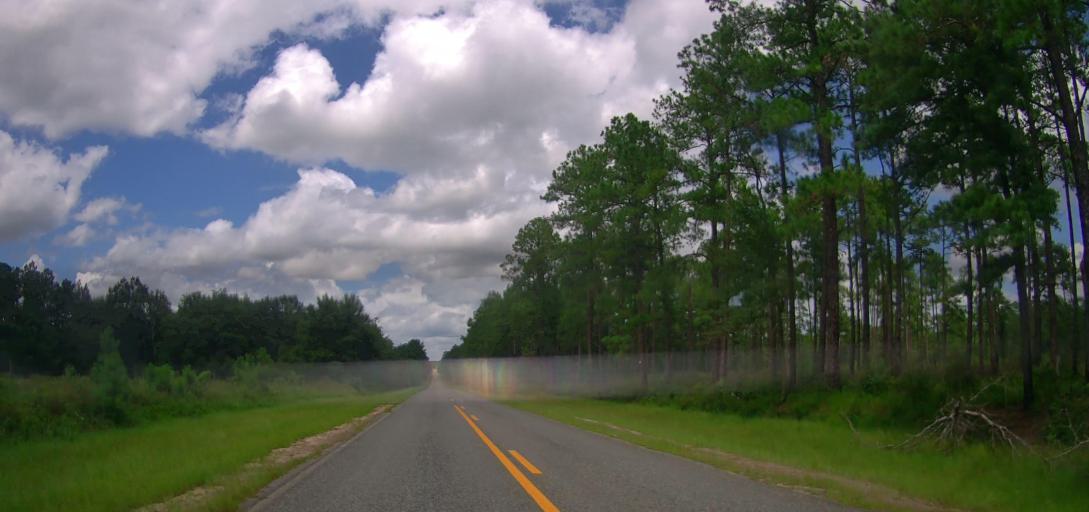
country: US
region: Georgia
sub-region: Turner County
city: Ashburn
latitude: 31.7144
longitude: -83.5055
